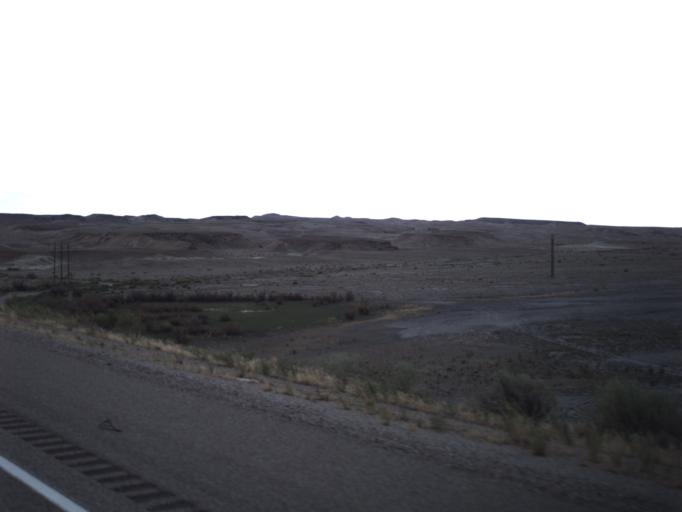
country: US
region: Utah
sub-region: Carbon County
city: East Carbon City
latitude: 38.9821
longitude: -110.1633
